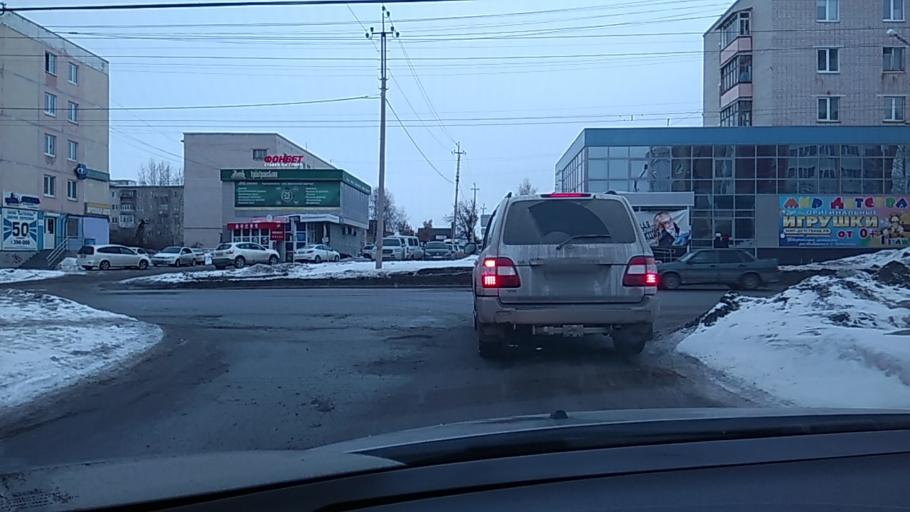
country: RU
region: Sverdlovsk
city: Kamensk-Ural'skiy
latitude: 56.4243
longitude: 61.9069
